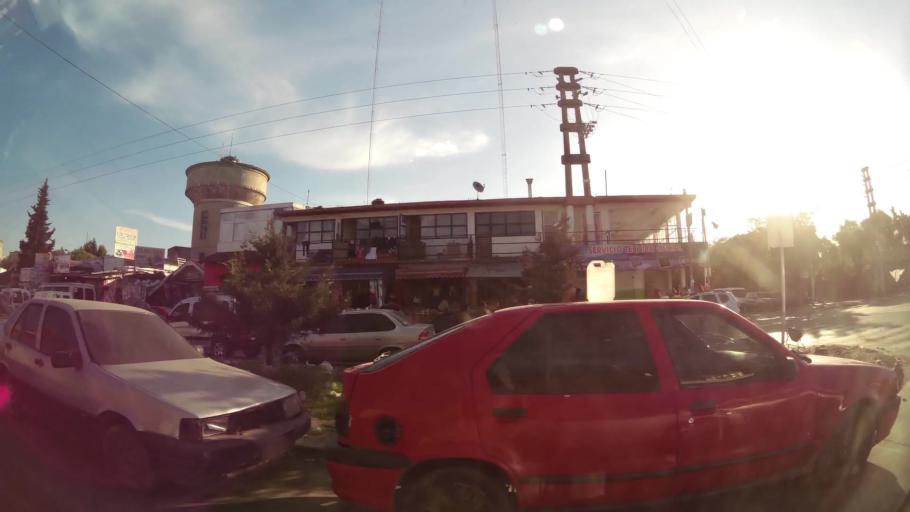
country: AR
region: Buenos Aires F.D.
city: Villa Lugano
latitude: -34.6981
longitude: -58.4873
